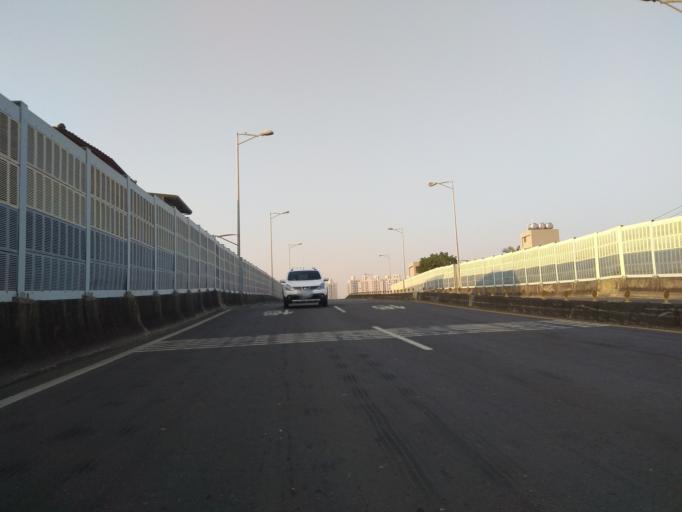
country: TW
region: Taiwan
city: Daxi
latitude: 24.9124
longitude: 121.1743
